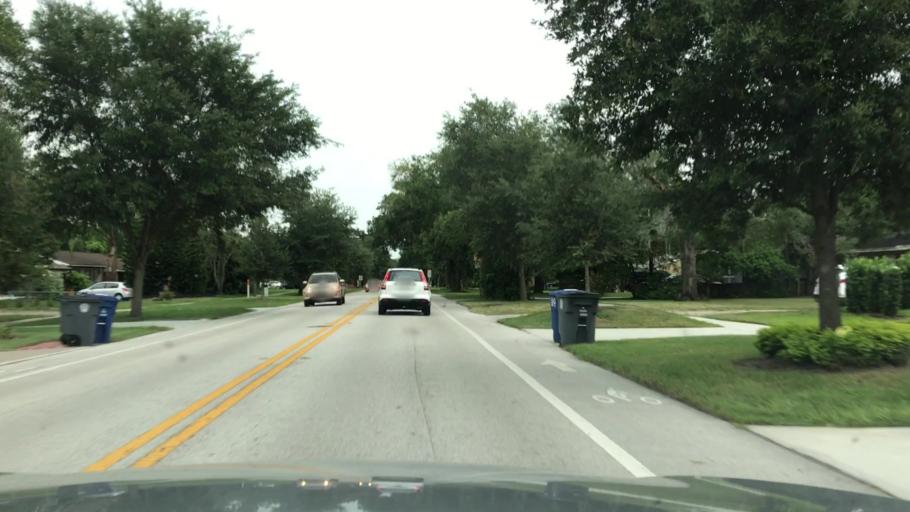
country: US
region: Florida
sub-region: Orange County
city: Winter Park
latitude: 28.5909
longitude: -81.3278
